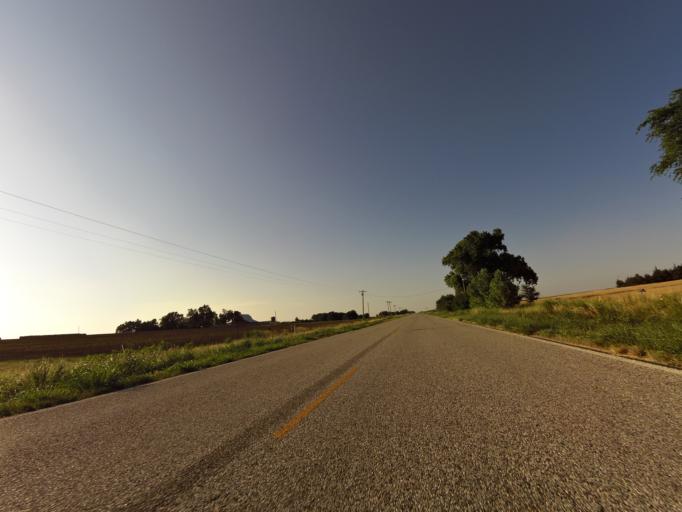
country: US
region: Kansas
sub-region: McPherson County
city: Inman
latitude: 38.1863
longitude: -97.8485
